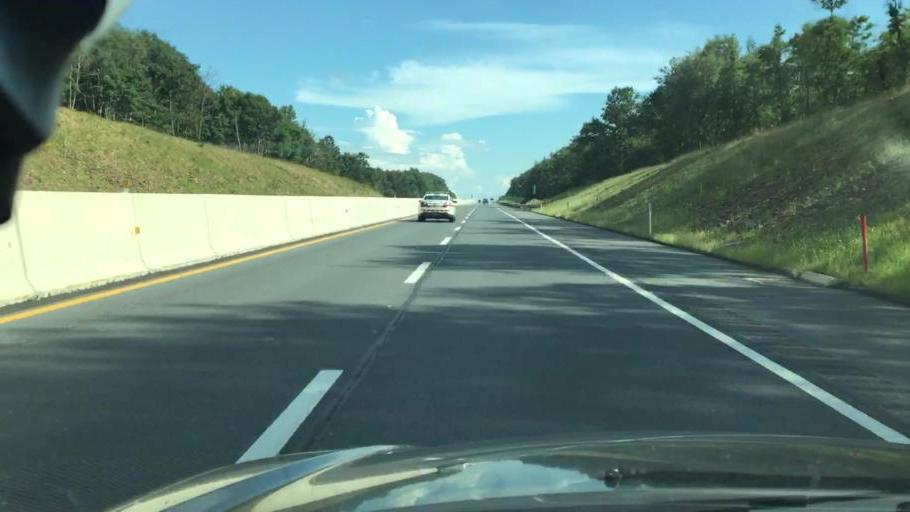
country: US
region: Pennsylvania
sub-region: Carbon County
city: Towamensing Trails
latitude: 41.0379
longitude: -75.6616
